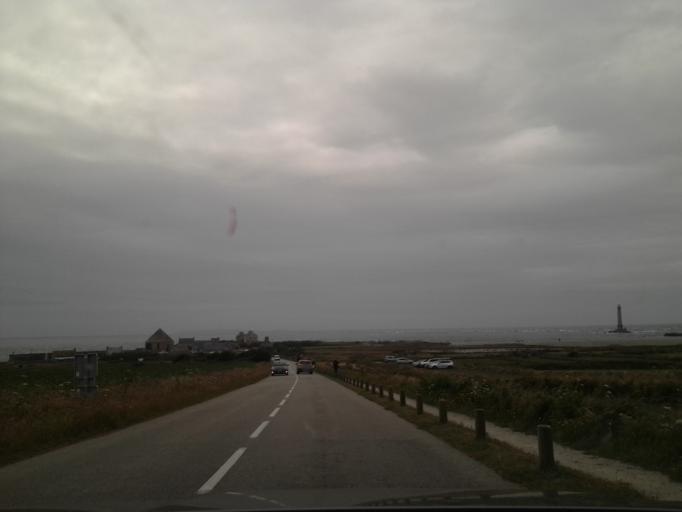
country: FR
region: Lower Normandy
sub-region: Departement de la Manche
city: Beaumont-Hague
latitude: 49.7158
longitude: -1.9387
